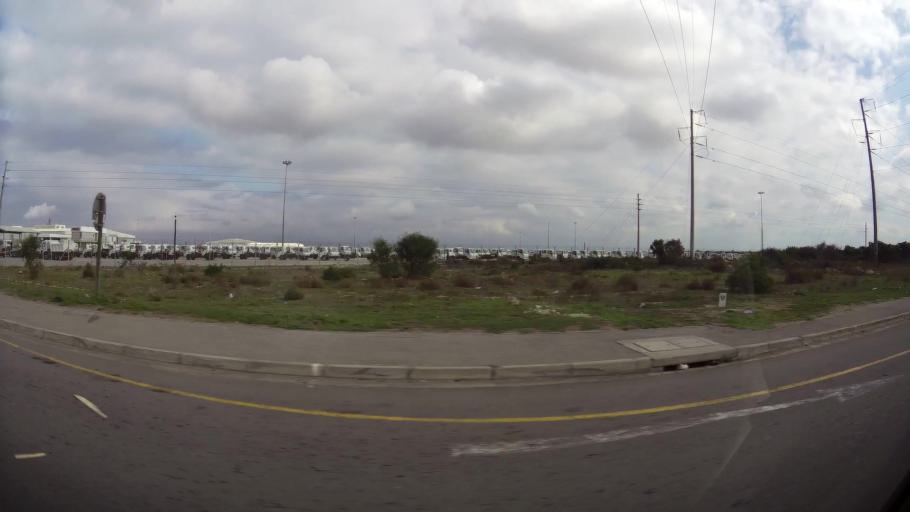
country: ZA
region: Eastern Cape
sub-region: Nelson Mandela Bay Metropolitan Municipality
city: Port Elizabeth
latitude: -33.8092
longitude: 25.6264
